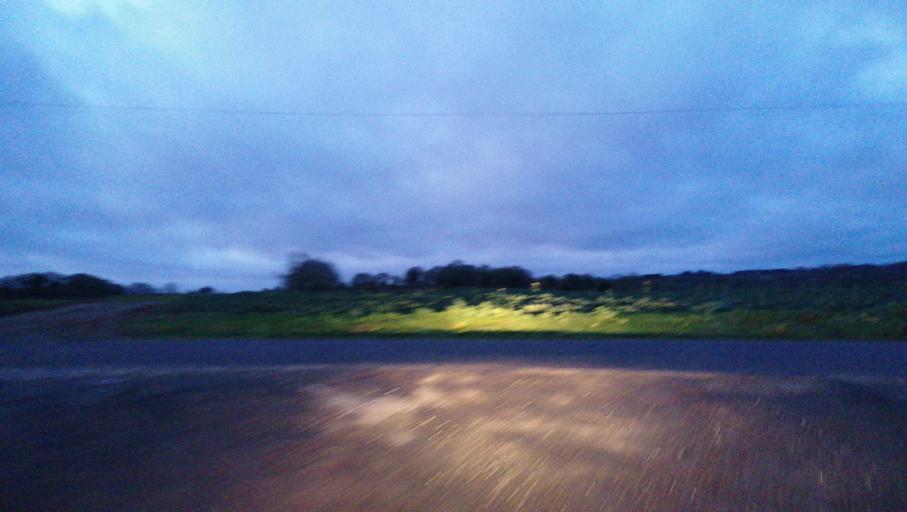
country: FR
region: Brittany
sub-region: Departement des Cotes-d'Armor
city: Plehedel
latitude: 48.6701
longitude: -3.0361
